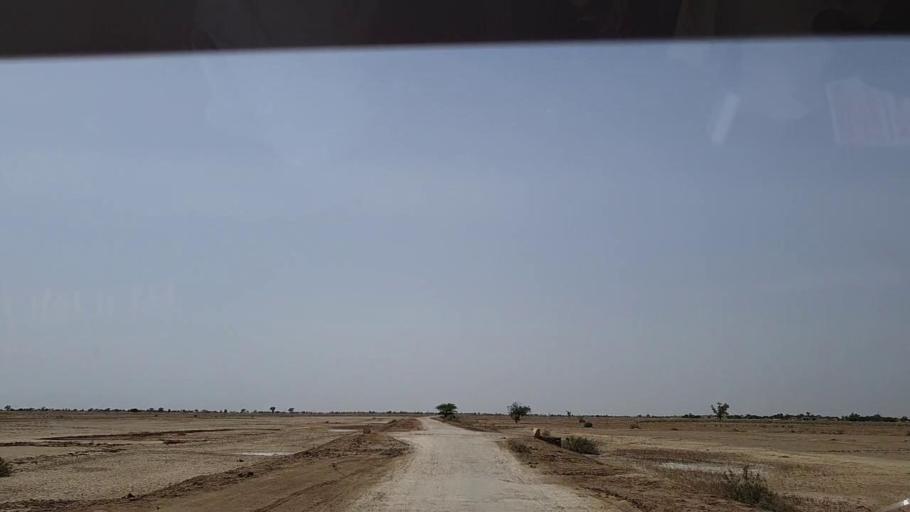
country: PK
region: Sindh
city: Johi
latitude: 26.7405
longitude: 67.6314
